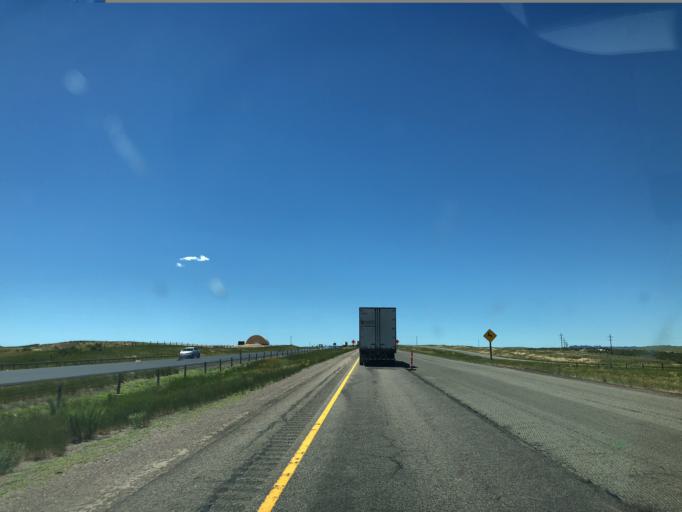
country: US
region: Wyoming
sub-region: Laramie County
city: Cheyenne
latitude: 41.0995
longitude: -105.1441
